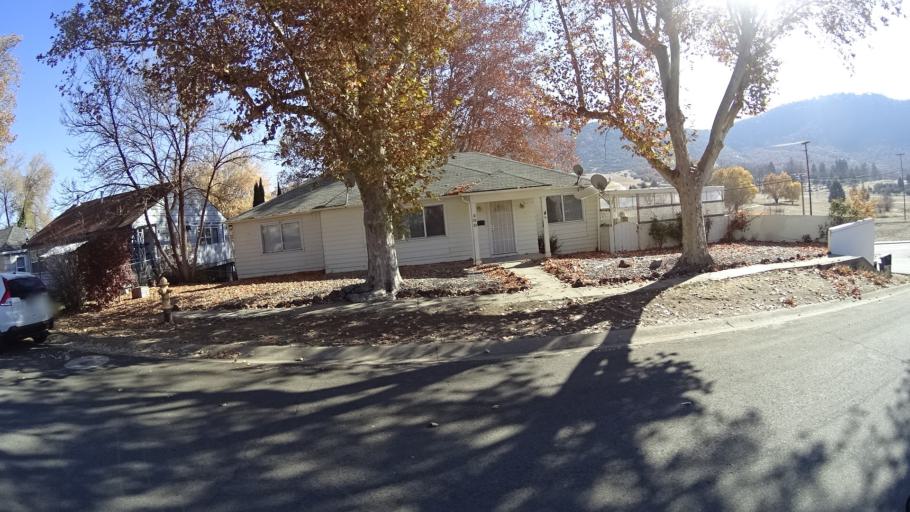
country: US
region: California
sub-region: Siskiyou County
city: Yreka
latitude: 41.7331
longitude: -122.6305
